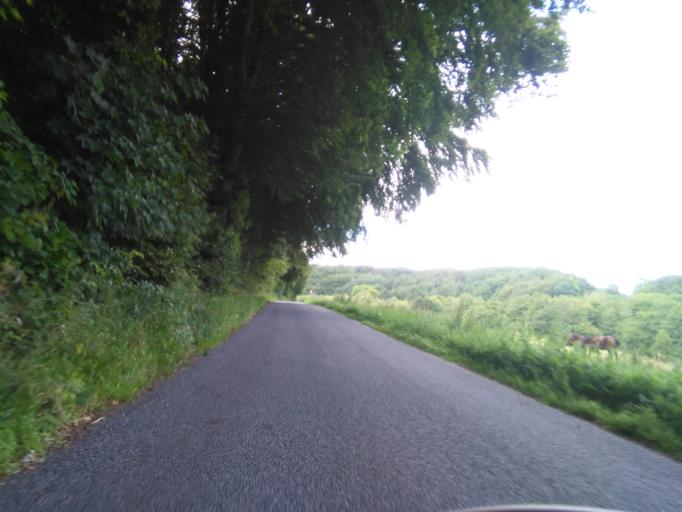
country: DK
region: Central Jutland
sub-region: Skanderborg Kommune
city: Horning
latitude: 56.1039
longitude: 10.0166
